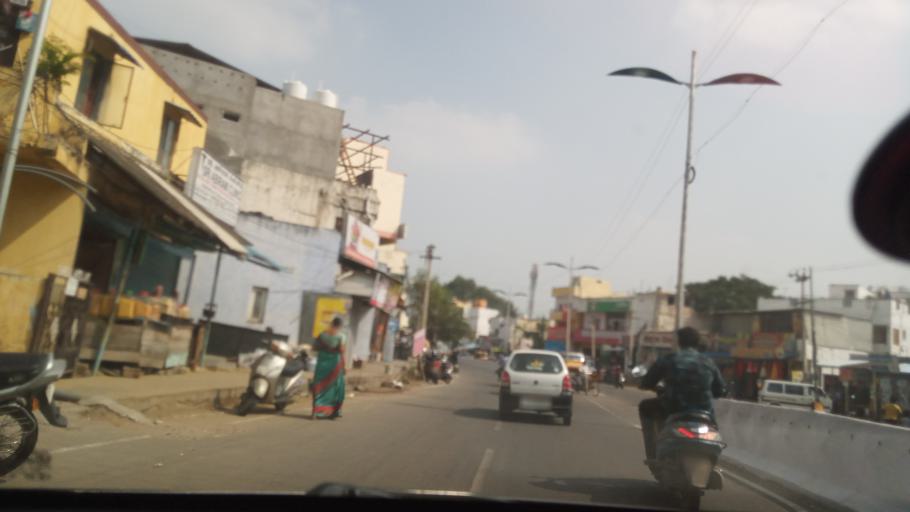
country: IN
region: Tamil Nadu
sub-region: Coimbatore
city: Perur
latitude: 11.0179
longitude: 76.9213
